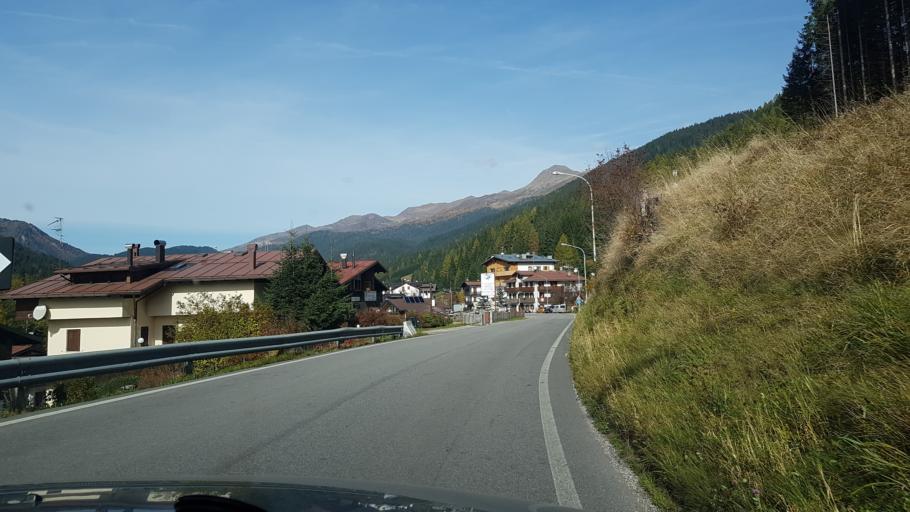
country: IT
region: Veneto
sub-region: Provincia di Belluno
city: Candide
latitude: 46.6067
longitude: 12.4818
